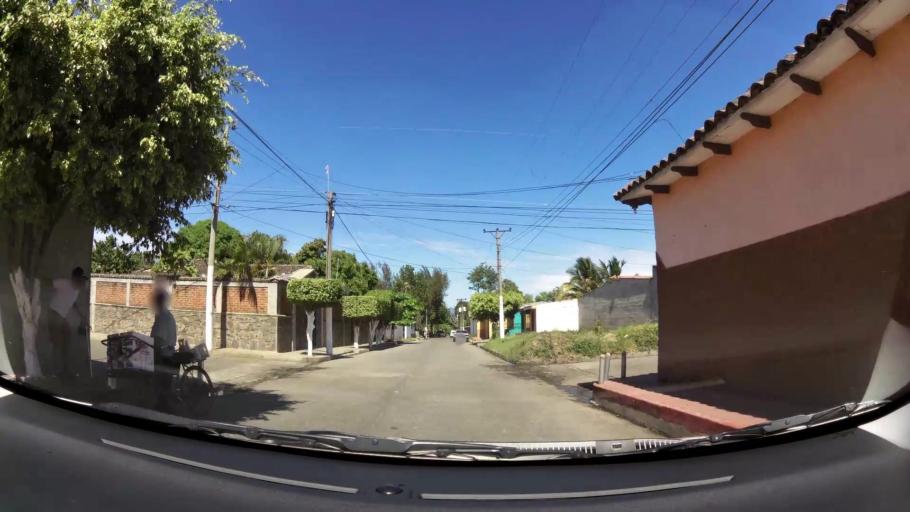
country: SV
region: Santa Ana
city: Chalchuapa
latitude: 13.9739
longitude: -89.7056
